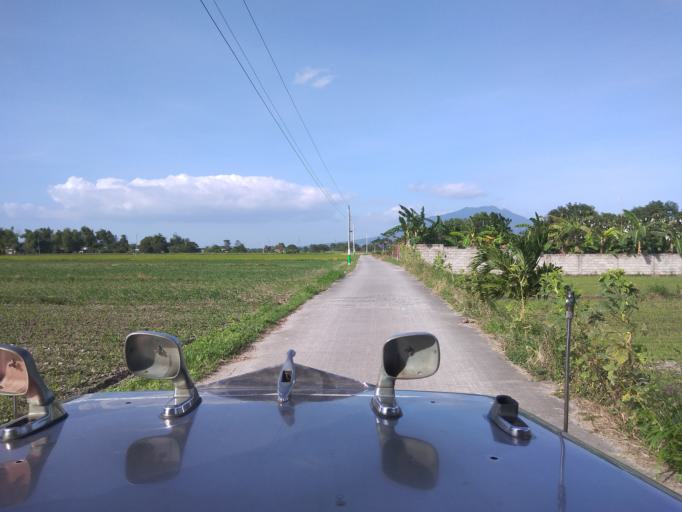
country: PH
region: Central Luzon
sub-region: Province of Pampanga
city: Bulaon
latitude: 15.0966
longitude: 120.6938
